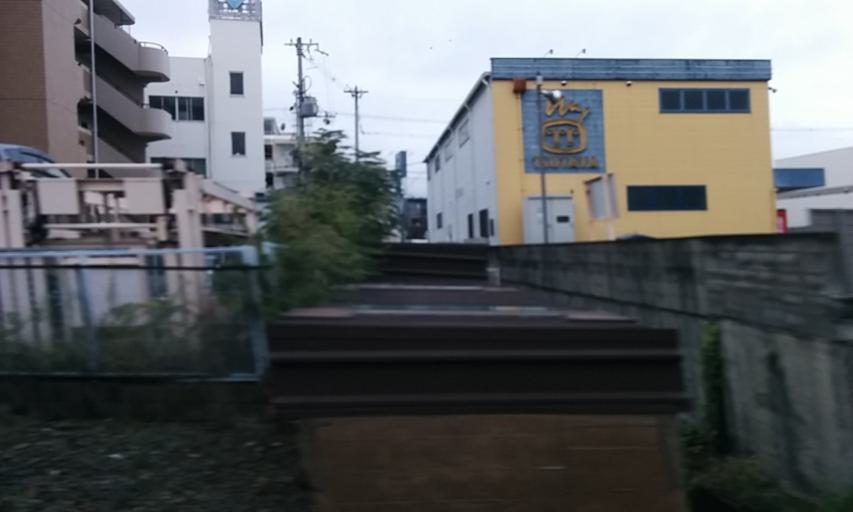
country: JP
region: Kyoto
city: Muko
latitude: 34.9210
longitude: 135.6909
